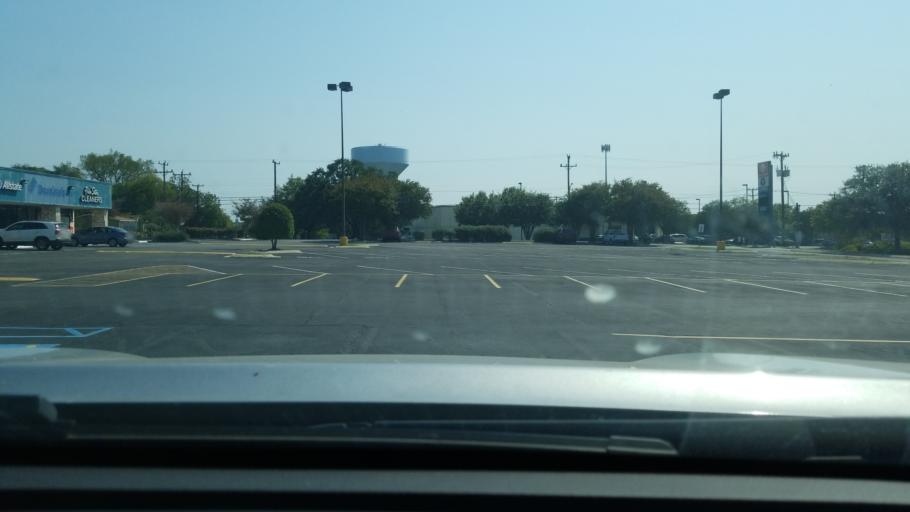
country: US
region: Texas
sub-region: Bexar County
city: Leon Valley
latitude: 29.5455
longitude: -98.6138
